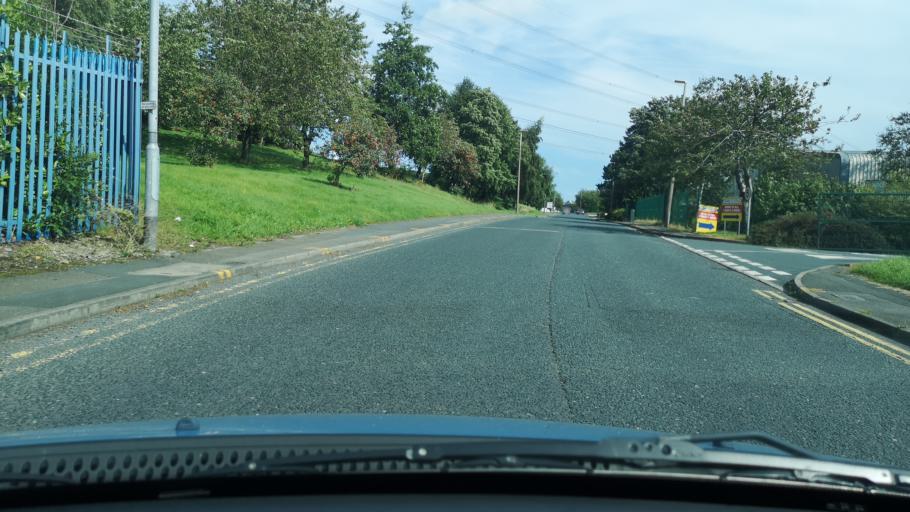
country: GB
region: England
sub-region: City and Borough of Leeds
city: Drighlington
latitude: 53.7412
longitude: -1.6518
